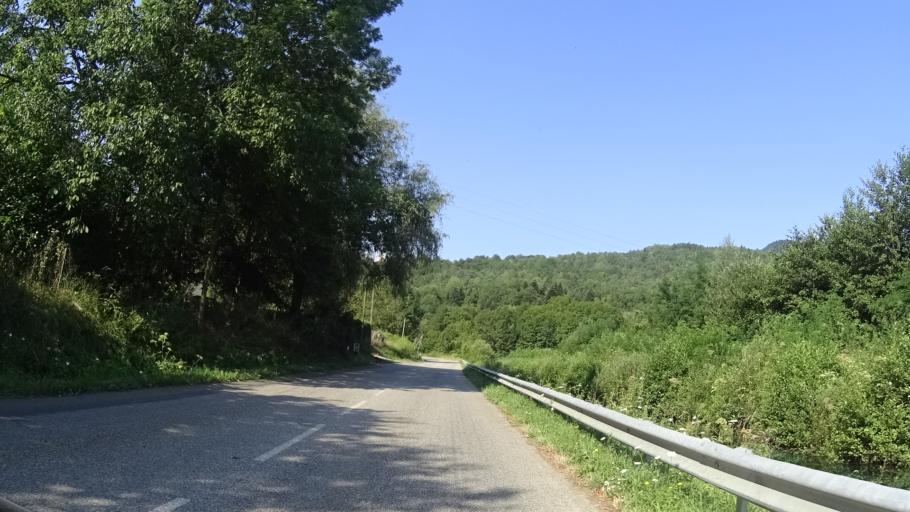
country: FR
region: Midi-Pyrenees
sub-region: Departement de l'Ariege
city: Belesta
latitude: 42.8972
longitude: 1.9297
